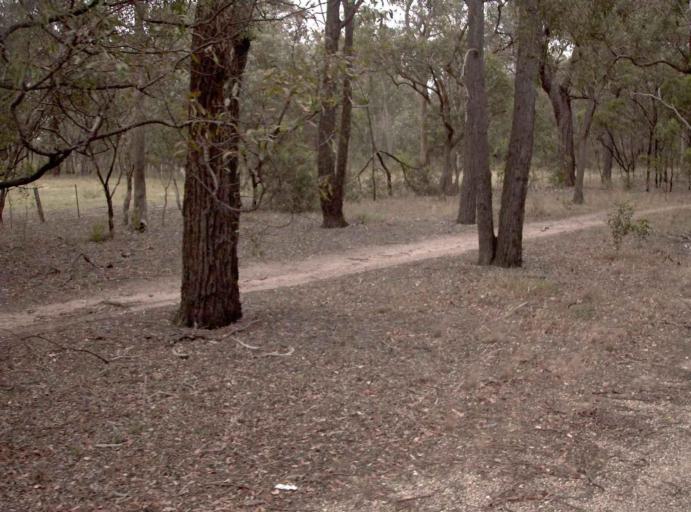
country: AU
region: Victoria
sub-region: Wellington
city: Heyfield
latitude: -37.9567
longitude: 146.7714
